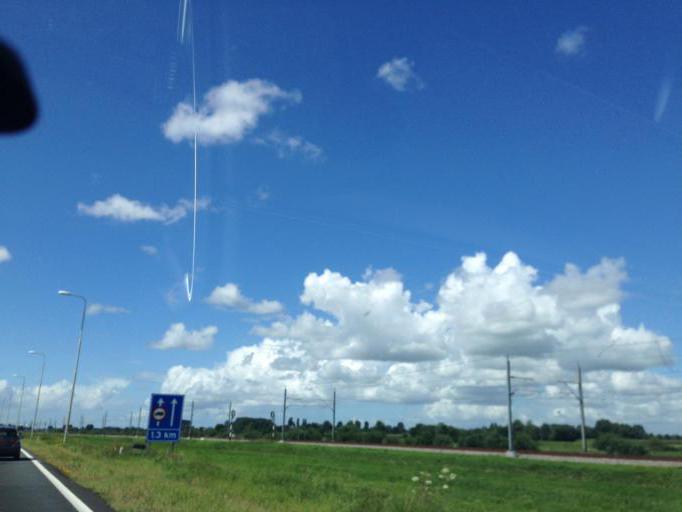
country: NL
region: Gelderland
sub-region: Gemeente Hattem
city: Hattem
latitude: 52.5022
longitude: 5.9941
